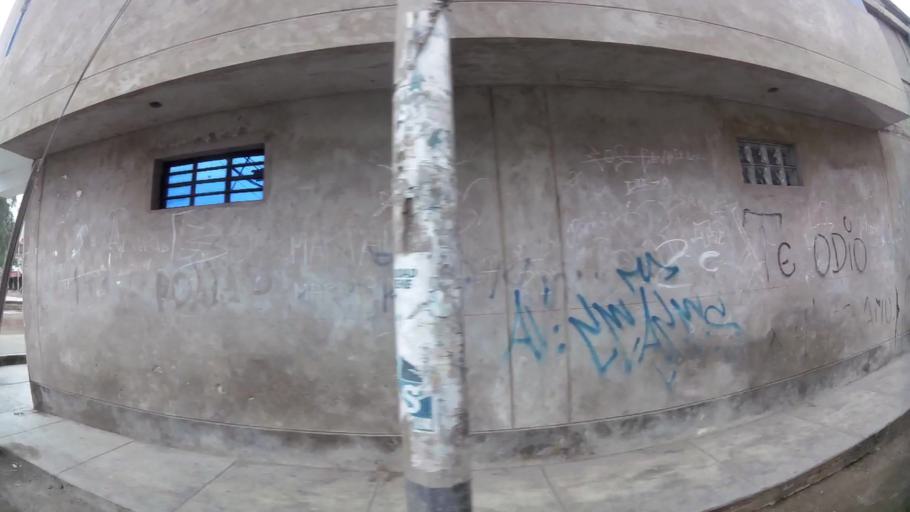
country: PE
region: Lima
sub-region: Lima
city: Cieneguilla
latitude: -12.2068
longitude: -76.9055
